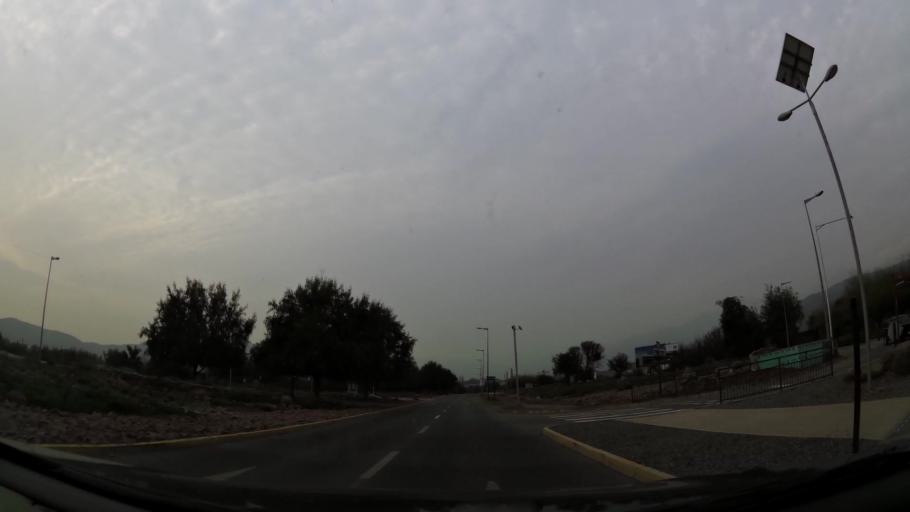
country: CL
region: Santiago Metropolitan
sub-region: Provincia de Chacabuco
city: Chicureo Abajo
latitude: -33.2723
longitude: -70.6247
